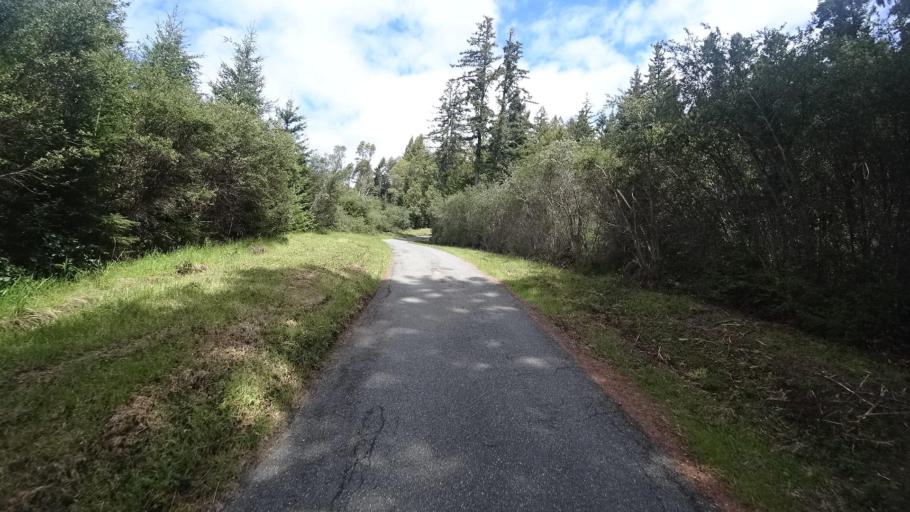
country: US
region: California
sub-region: Humboldt County
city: Blue Lake
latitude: 40.7805
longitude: -123.9628
